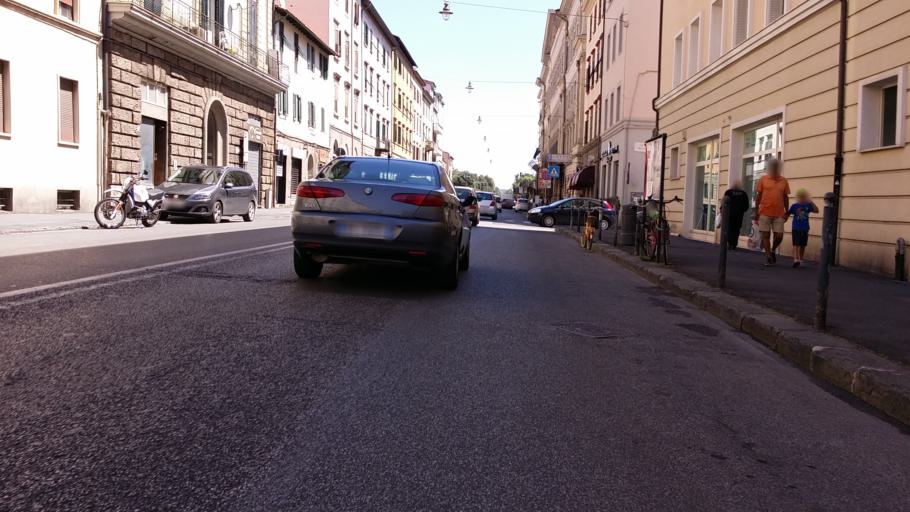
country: IT
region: Tuscany
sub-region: Provincia di Livorno
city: Livorno
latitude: 43.5525
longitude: 10.3162
